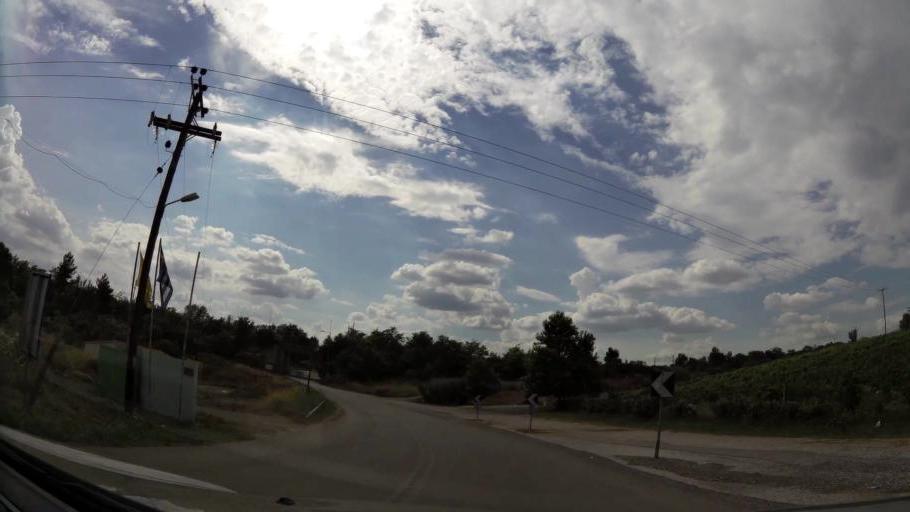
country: GR
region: Central Macedonia
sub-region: Nomos Pierias
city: Makrygialos
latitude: 40.4172
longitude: 22.5936
